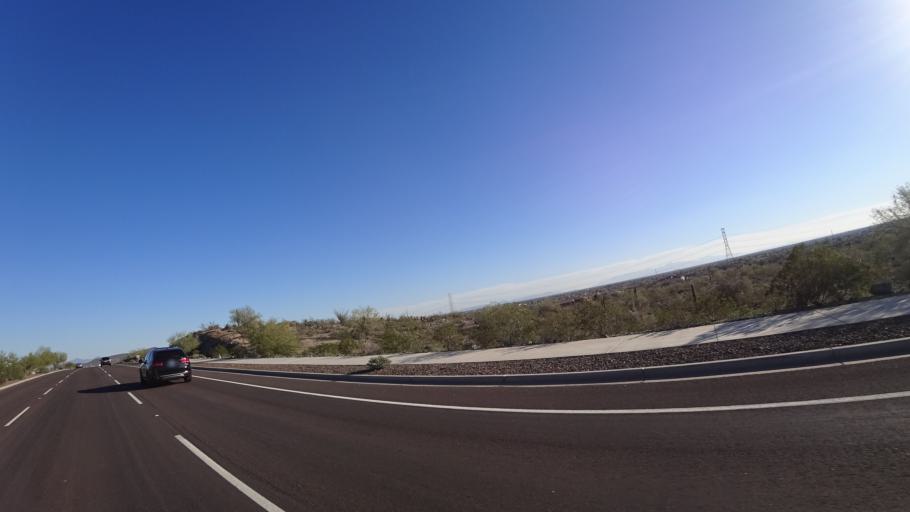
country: US
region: Arizona
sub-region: Maricopa County
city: Sun City West
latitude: 33.7105
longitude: -112.2455
